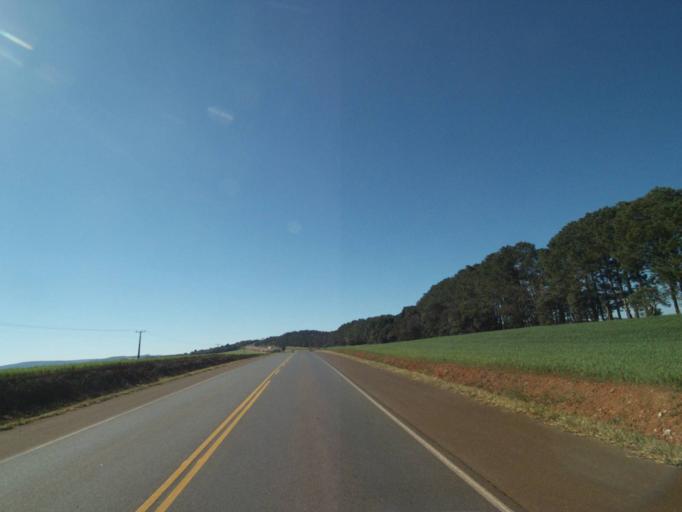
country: BR
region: Parana
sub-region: Tibagi
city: Tibagi
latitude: -24.4197
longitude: -50.3708
